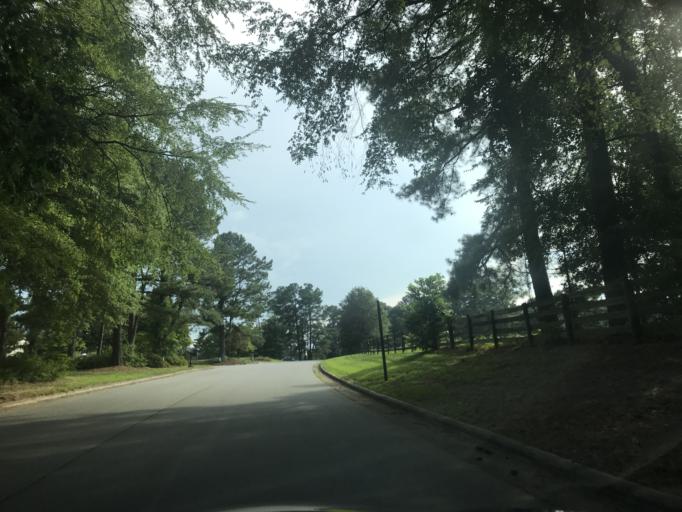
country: US
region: North Carolina
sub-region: Wake County
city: Knightdale
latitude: 35.8219
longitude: -78.5466
